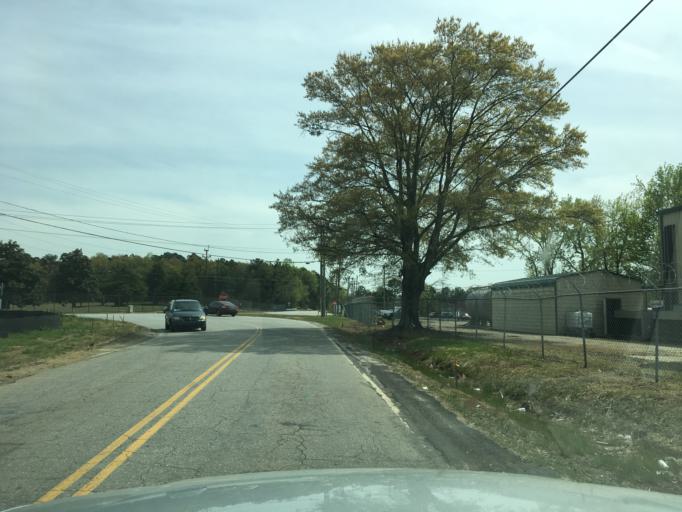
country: US
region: South Carolina
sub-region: Spartanburg County
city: Fairforest
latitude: 34.9466
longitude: -82.0064
